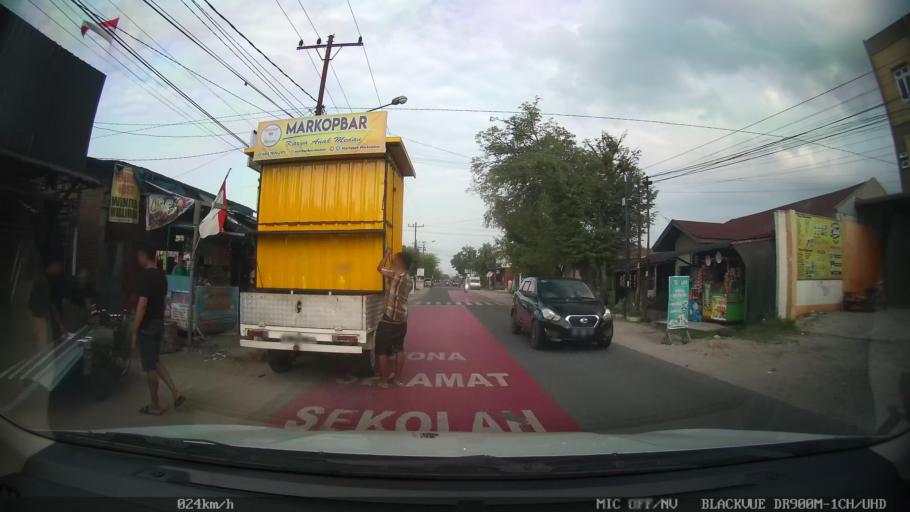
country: ID
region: North Sumatra
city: Sunggal
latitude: 3.5630
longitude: 98.6180
